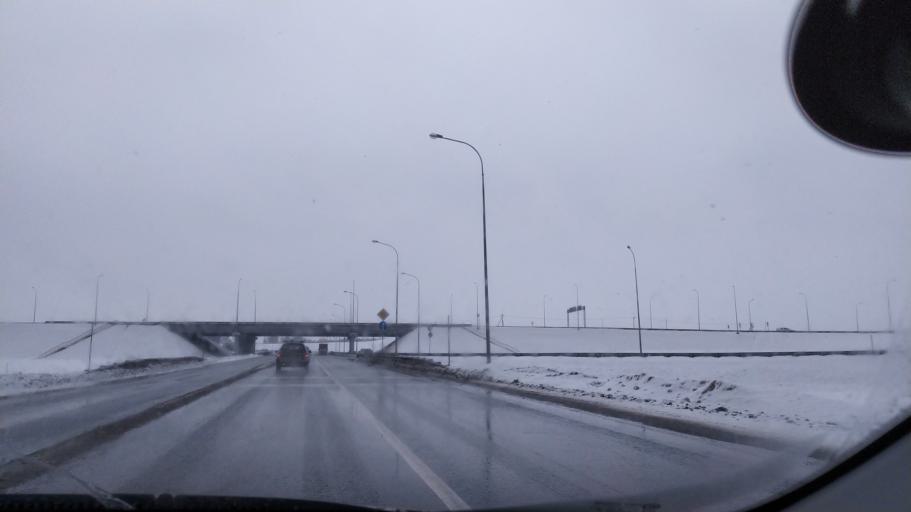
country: RU
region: Tatarstan
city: Aysha
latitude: 55.8728
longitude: 48.6603
